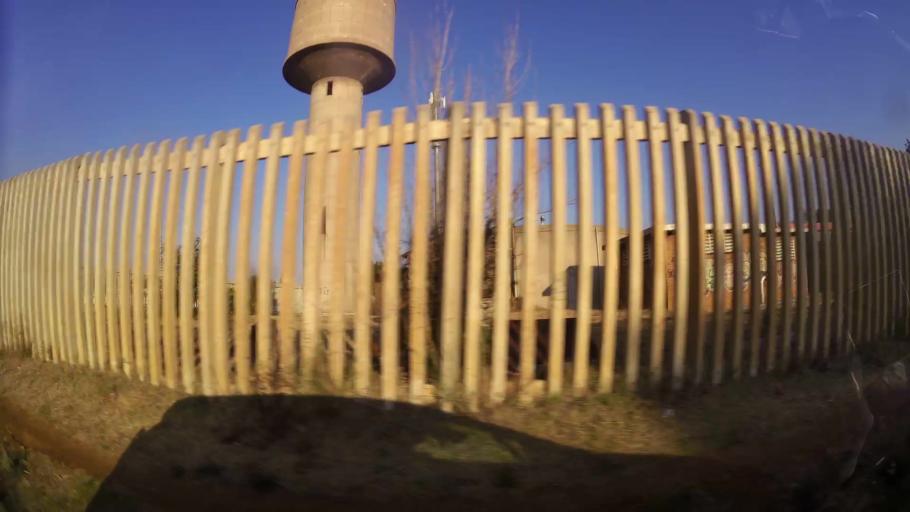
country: ZA
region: Gauteng
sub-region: Ekurhuleni Metropolitan Municipality
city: Boksburg
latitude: -26.2623
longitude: 28.2334
